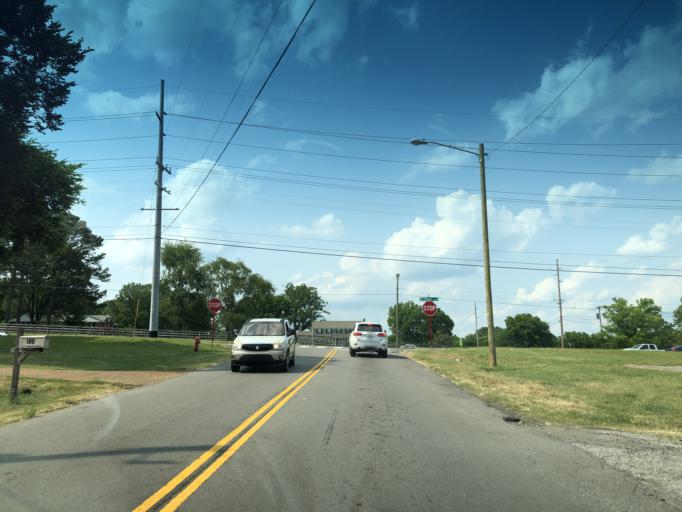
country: US
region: Tennessee
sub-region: Davidson County
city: Goodlettsville
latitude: 36.2637
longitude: -86.7272
